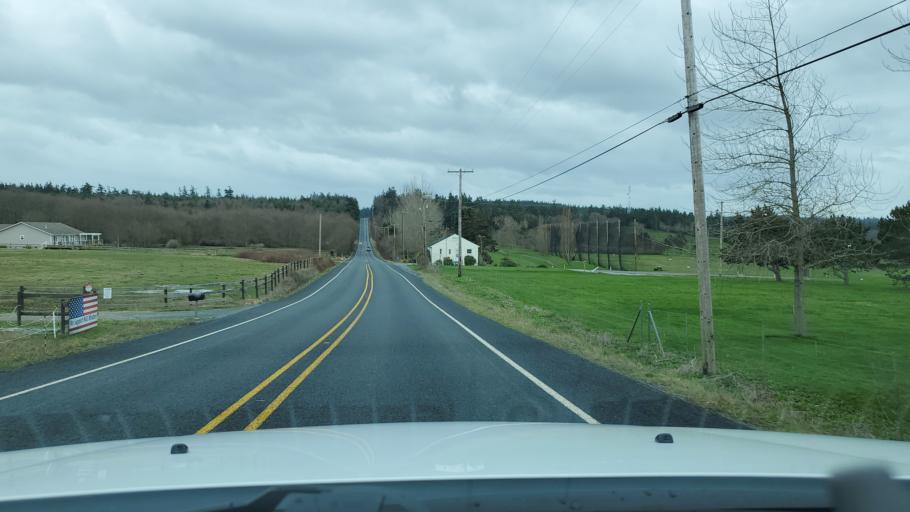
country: US
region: Washington
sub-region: Island County
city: Ault Field
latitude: 48.3219
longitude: -122.6911
